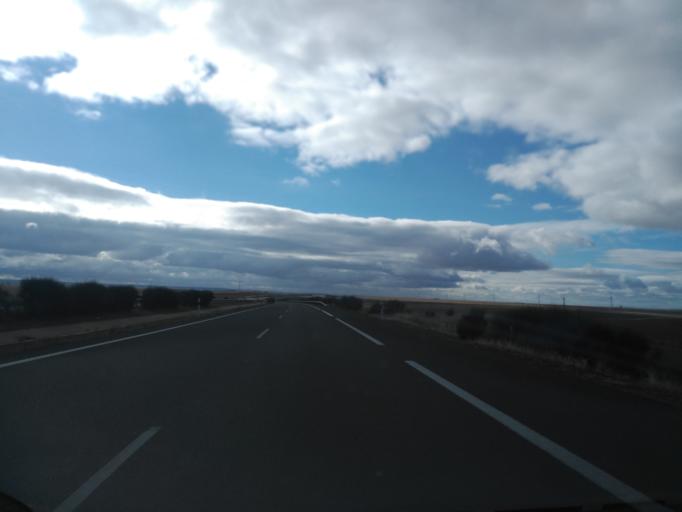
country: ES
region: Castille and Leon
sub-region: Provincia de Palencia
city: Marcilla de Campos
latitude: 42.3403
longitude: -4.3927
